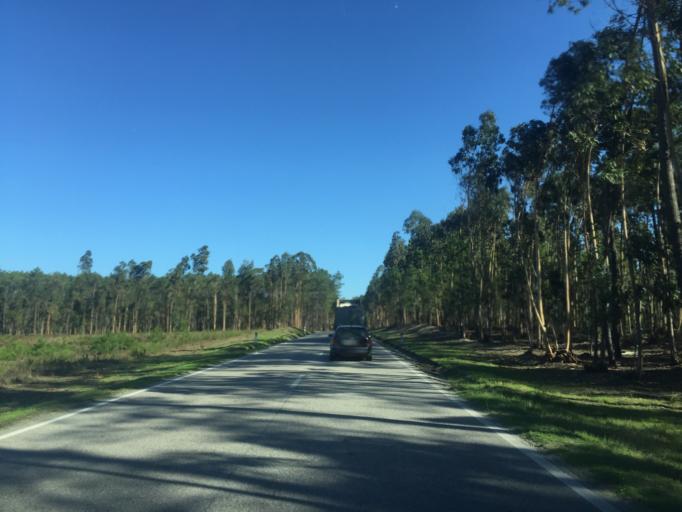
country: PT
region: Leiria
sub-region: Leiria
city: Monte Redondo
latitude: 39.9282
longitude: -8.8048
